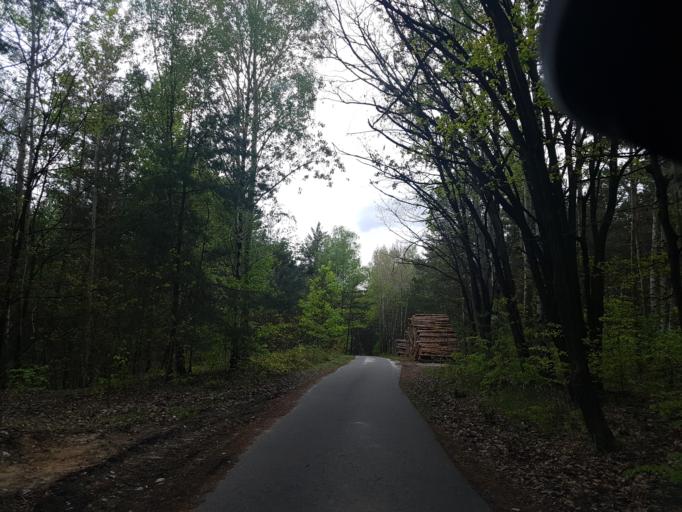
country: DE
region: Brandenburg
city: Tschernitz
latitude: 51.6101
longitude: 14.5847
